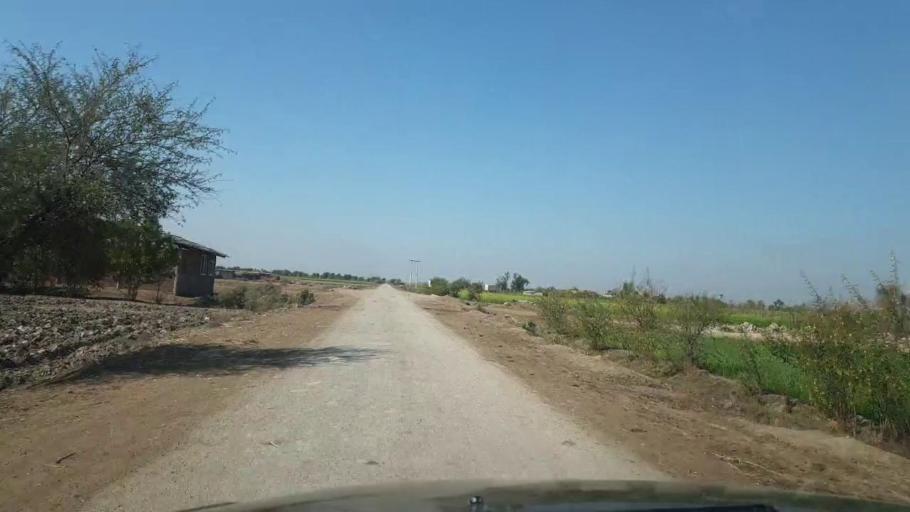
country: PK
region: Sindh
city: Mirpur Khas
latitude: 25.5864
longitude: 69.0717
